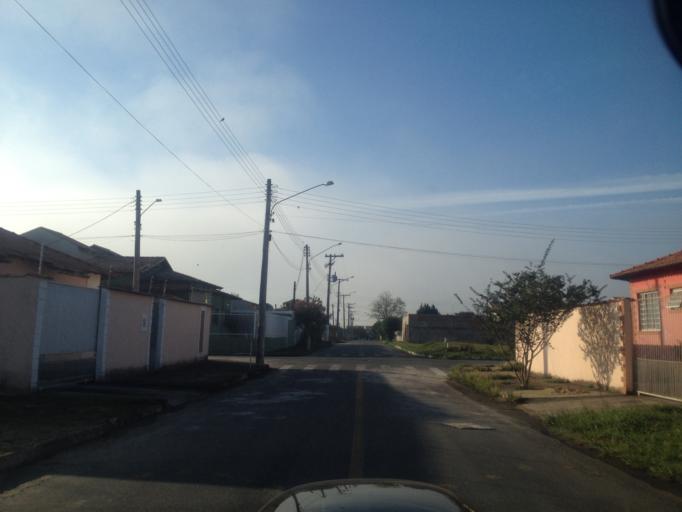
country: BR
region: Rio de Janeiro
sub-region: Porto Real
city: Porto Real
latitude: -22.4102
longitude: -44.3122
